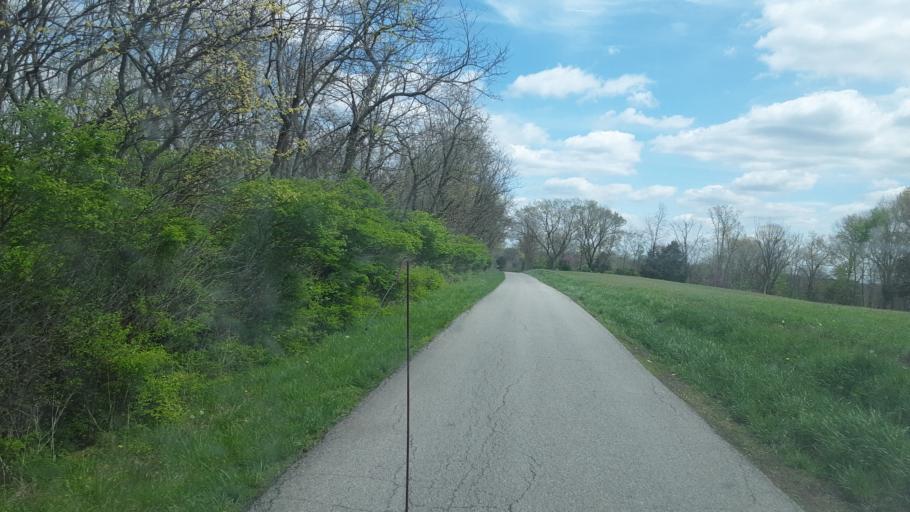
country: US
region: Kentucky
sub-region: Owen County
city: Owenton
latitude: 38.6752
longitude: -84.8043
